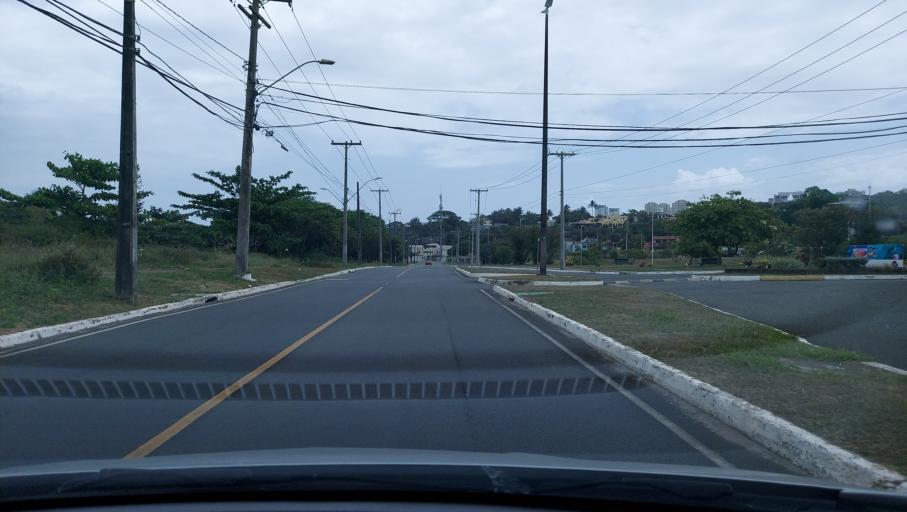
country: BR
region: Bahia
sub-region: Lauro De Freitas
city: Lauro de Freitas
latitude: -12.9513
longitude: -38.3919
